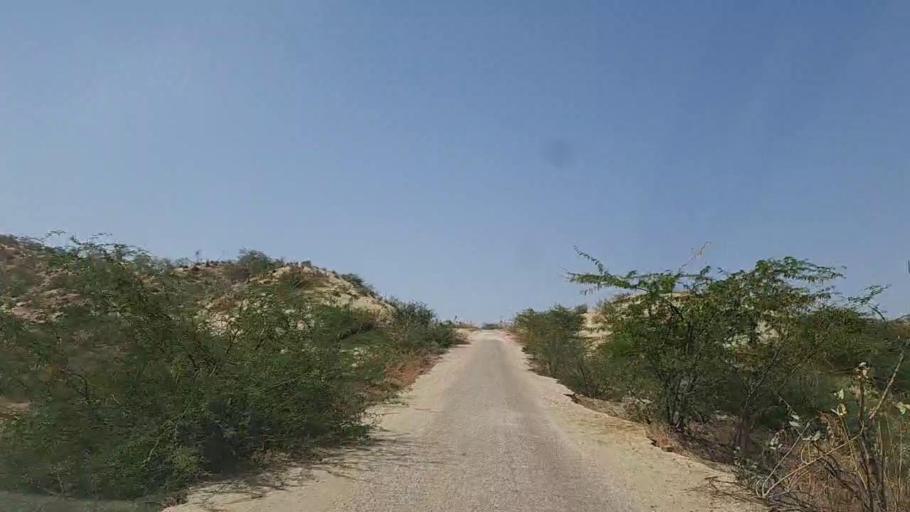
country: PK
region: Sindh
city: Diplo
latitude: 24.5351
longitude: 69.3892
